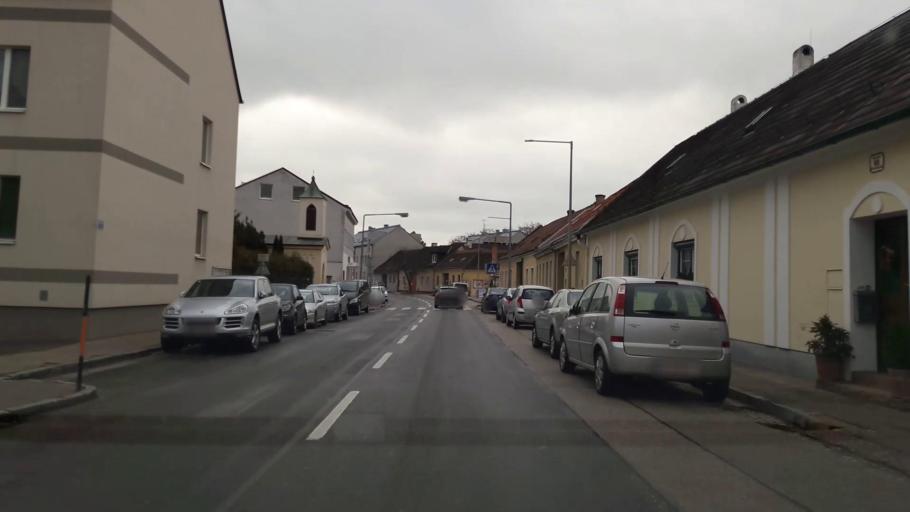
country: AT
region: Lower Austria
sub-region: Politischer Bezirk Wien-Umgebung
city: Lanzendorf
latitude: 48.1114
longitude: 16.4452
